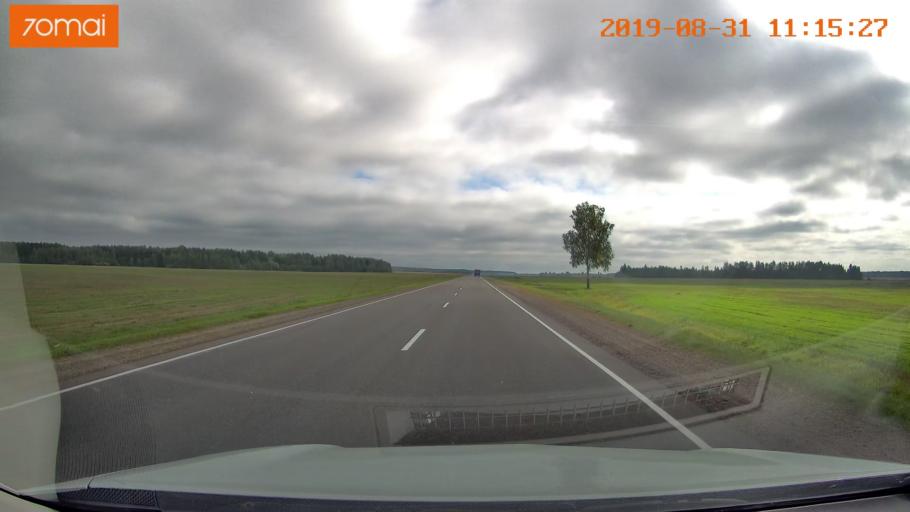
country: BY
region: Mogilev
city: Chavusy
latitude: 53.8098
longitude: 30.8584
